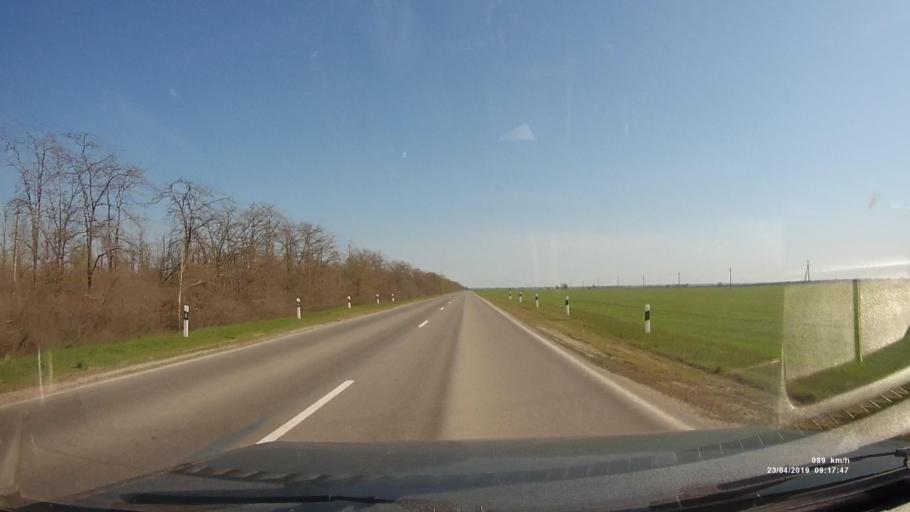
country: RU
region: Rostov
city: Proletarsk
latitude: 46.6568
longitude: 41.6814
